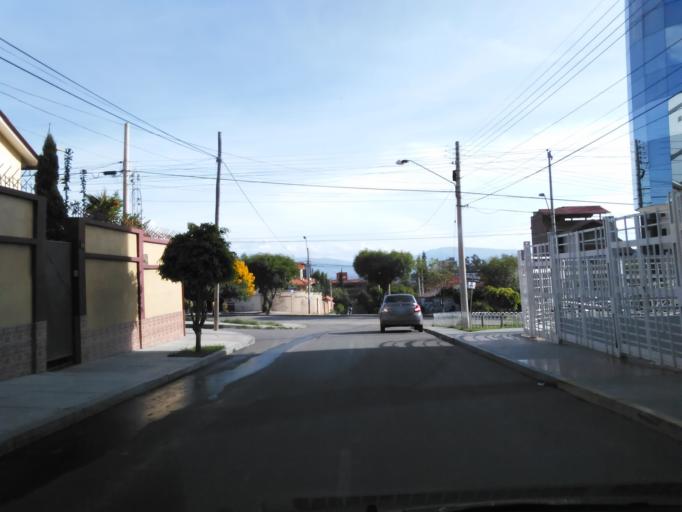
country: BO
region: Cochabamba
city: Cochabamba
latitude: -17.3676
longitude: -66.1468
